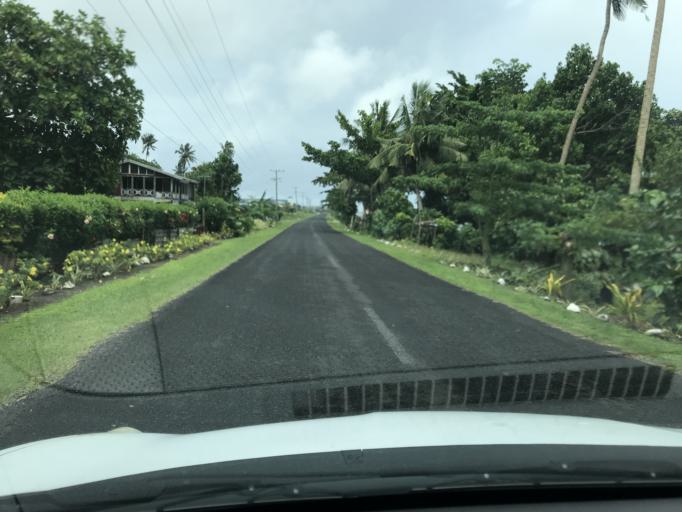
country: WS
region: Va`a-o-Fonoti
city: Samamea
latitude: -14.0433
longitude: -171.4371
